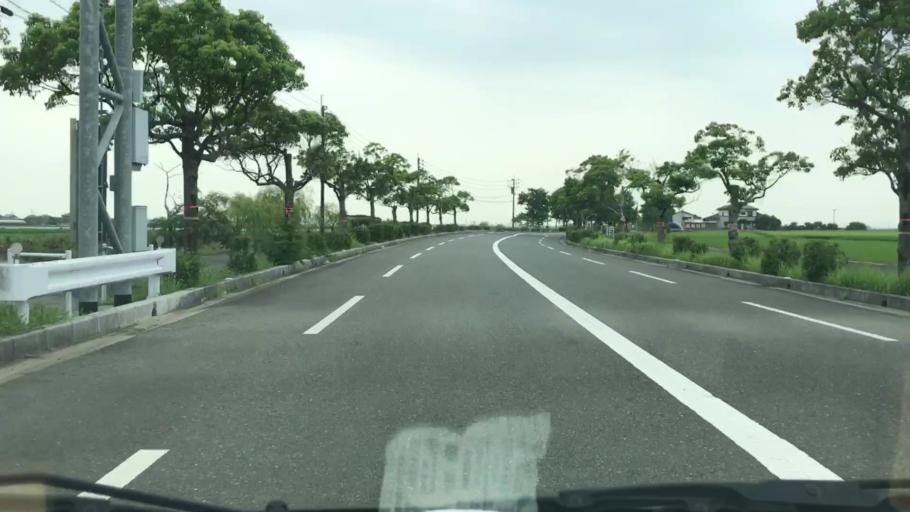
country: JP
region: Saga Prefecture
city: Okawa
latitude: 33.1934
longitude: 130.3036
